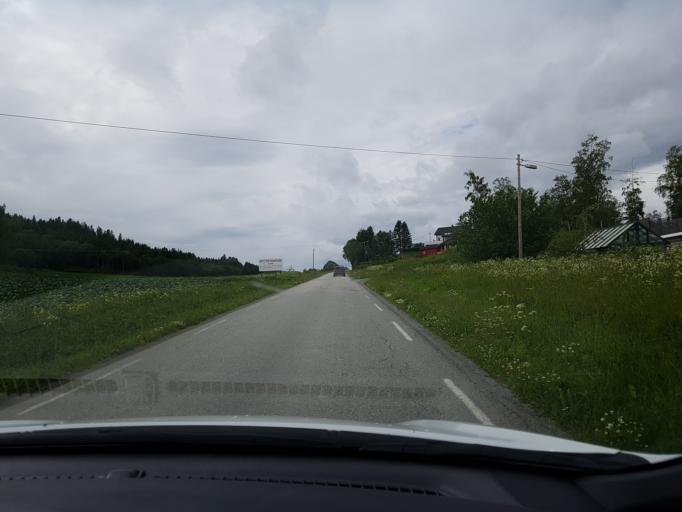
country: NO
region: Nord-Trondelag
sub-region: Frosta
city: Frosta
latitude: 63.6316
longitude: 10.7792
